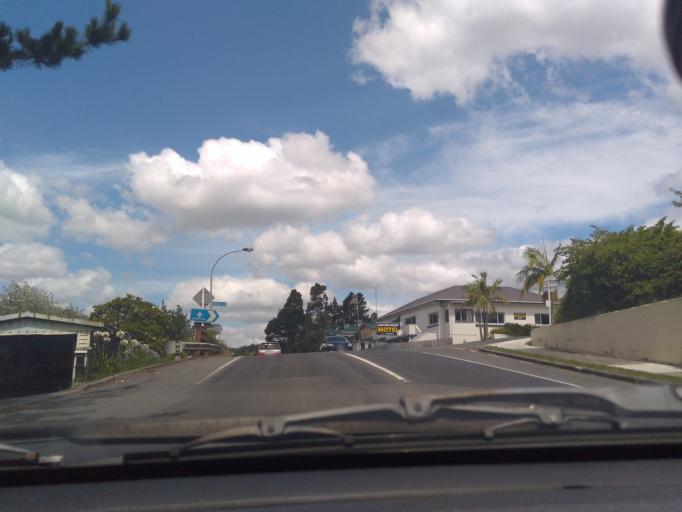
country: NZ
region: Northland
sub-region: Far North District
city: Kawakawa
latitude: -35.3802
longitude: 174.0694
